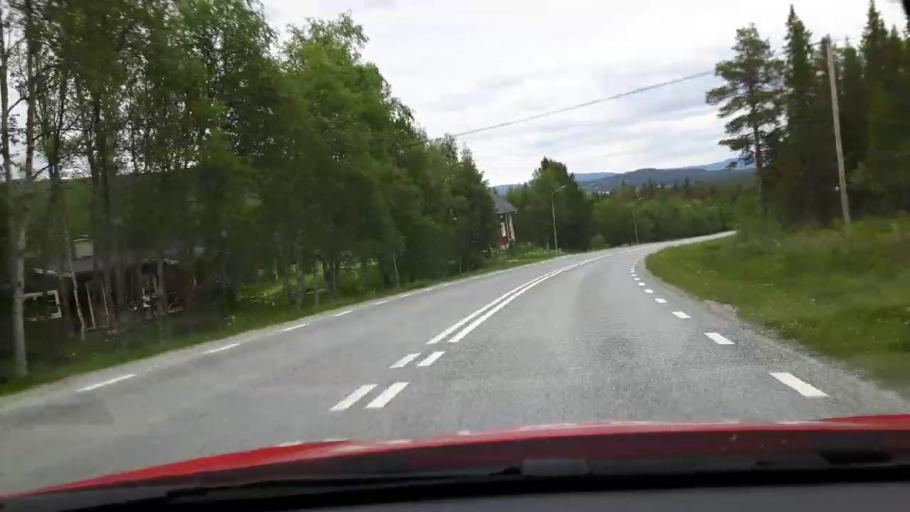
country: NO
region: Hedmark
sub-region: Engerdal
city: Engerdal
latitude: 62.5473
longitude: 12.4756
